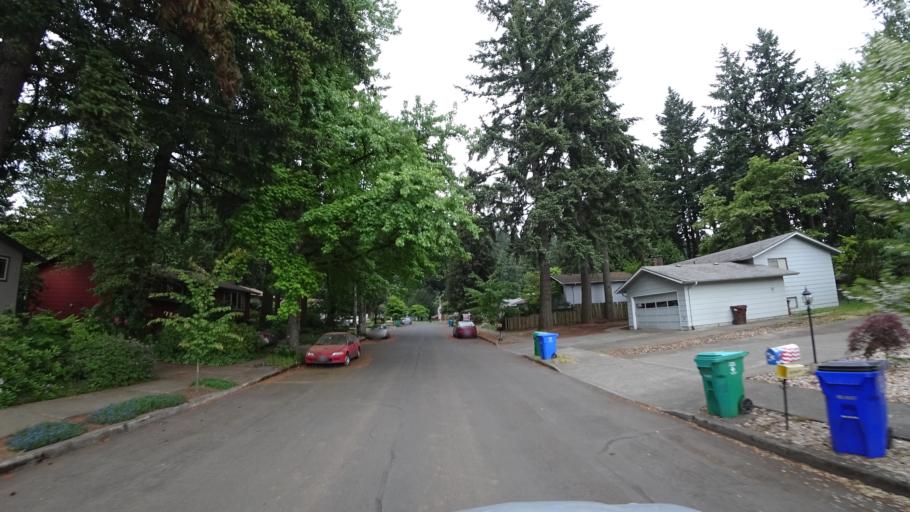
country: US
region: Oregon
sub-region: Clackamas County
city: Happy Valley
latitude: 45.4953
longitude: -122.5061
